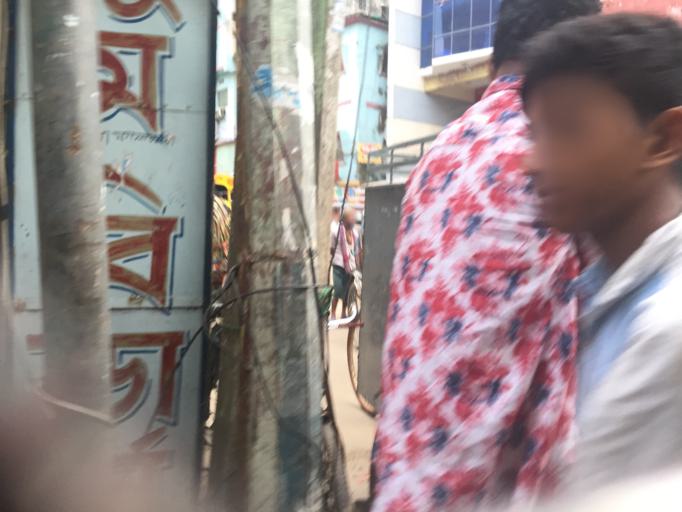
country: BD
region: Dhaka
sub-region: Dhaka
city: Dhaka
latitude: 23.7141
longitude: 90.4114
